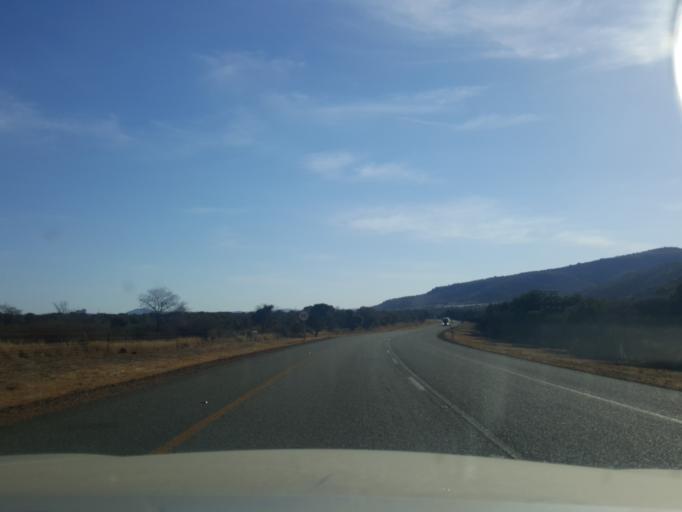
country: ZA
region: North-West
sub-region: Ngaka Modiri Molema District Municipality
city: Zeerust
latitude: -25.5422
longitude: 26.1161
